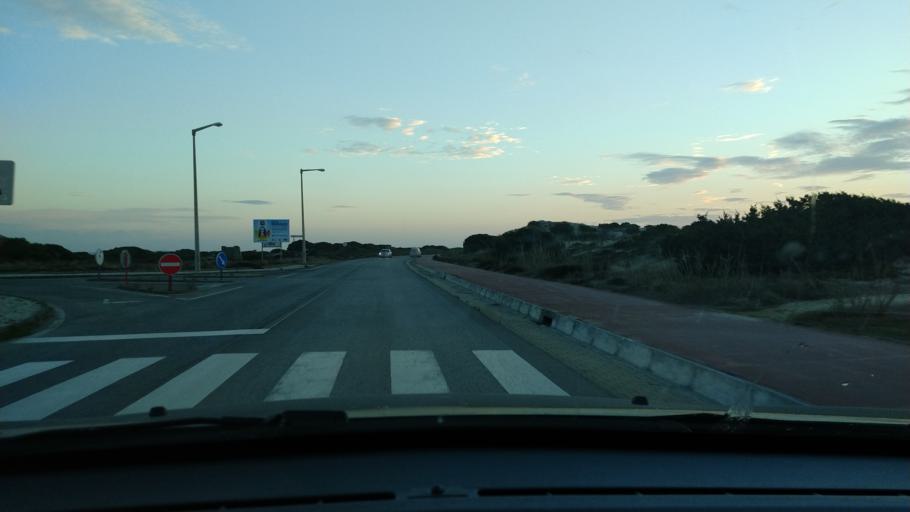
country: PT
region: Leiria
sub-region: Peniche
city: Atouguia da Baleia
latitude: 39.3640
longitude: -9.3381
